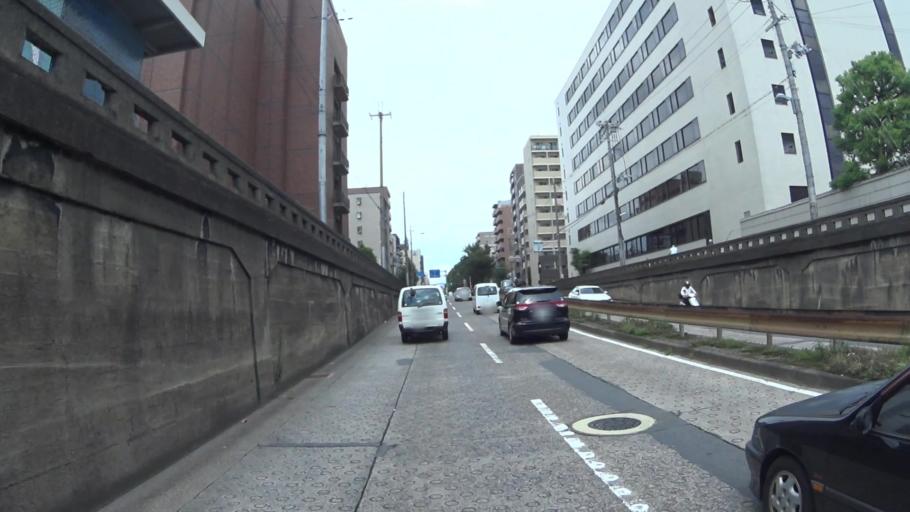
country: JP
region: Kyoto
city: Muko
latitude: 34.9821
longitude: 135.7326
